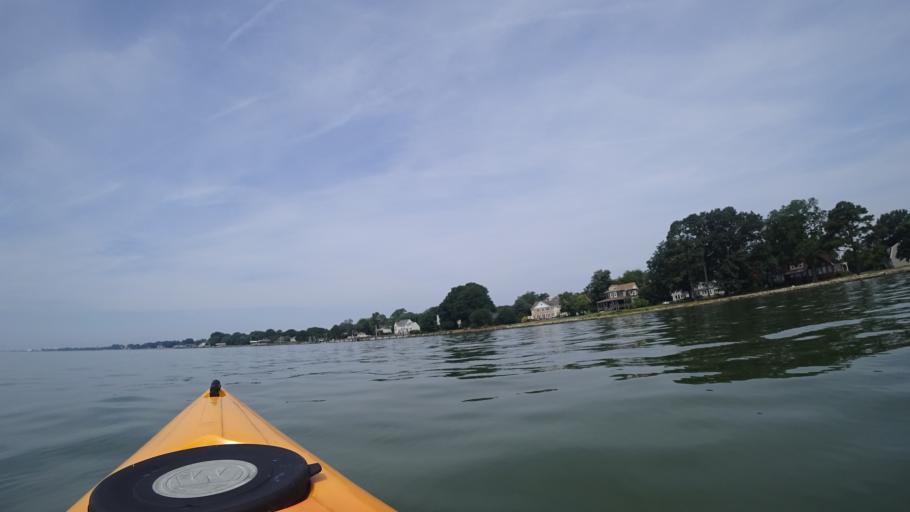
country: US
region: Virginia
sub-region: City of Hampton
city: Hampton
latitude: 36.9982
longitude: -76.3731
